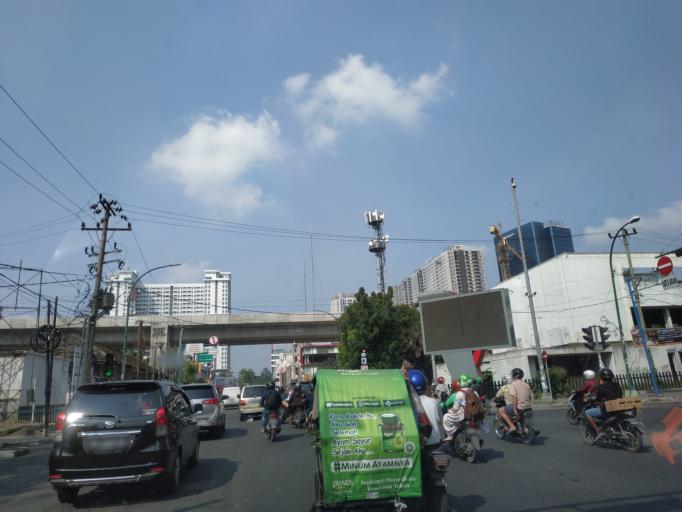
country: ID
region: North Sumatra
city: Medan
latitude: 3.5940
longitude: 98.6796
